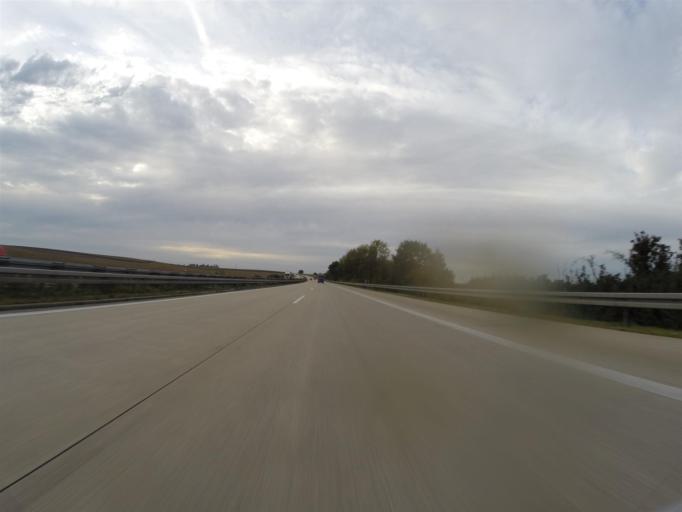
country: DE
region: Saxony
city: Ostrau
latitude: 51.2335
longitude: 12.8883
